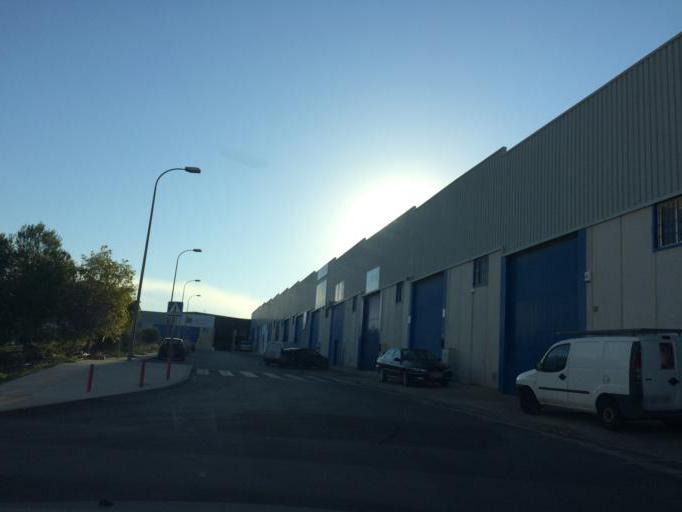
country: ES
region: Andalusia
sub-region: Provincia de Almeria
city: Viator
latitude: 36.8791
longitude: -2.4151
